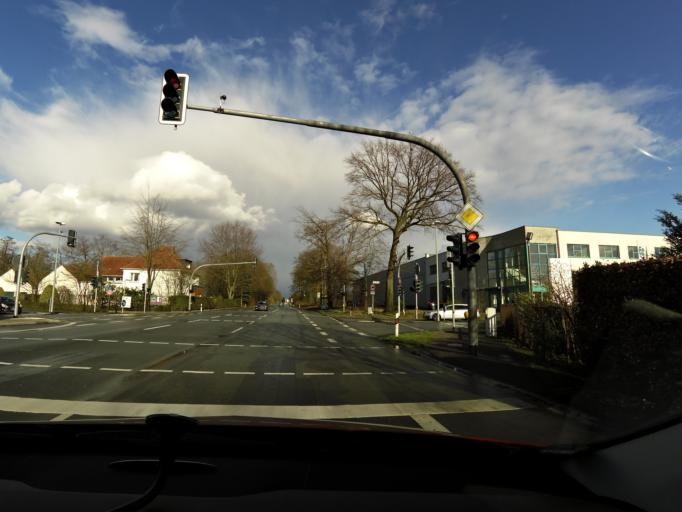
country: DE
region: North Rhine-Westphalia
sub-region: Regierungsbezirk Detmold
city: Verl
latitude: 51.8771
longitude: 8.4711
